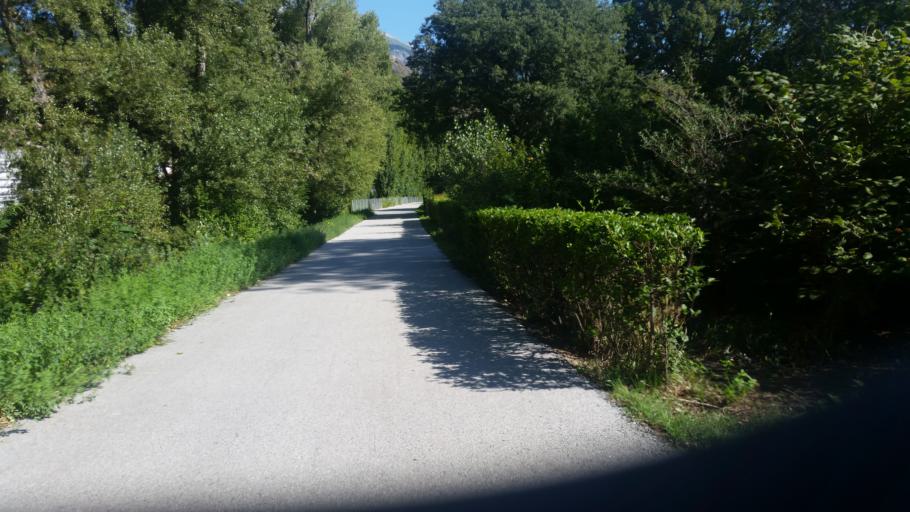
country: CH
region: Valais
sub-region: Sion District
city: Sitten
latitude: 46.2298
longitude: 7.3704
